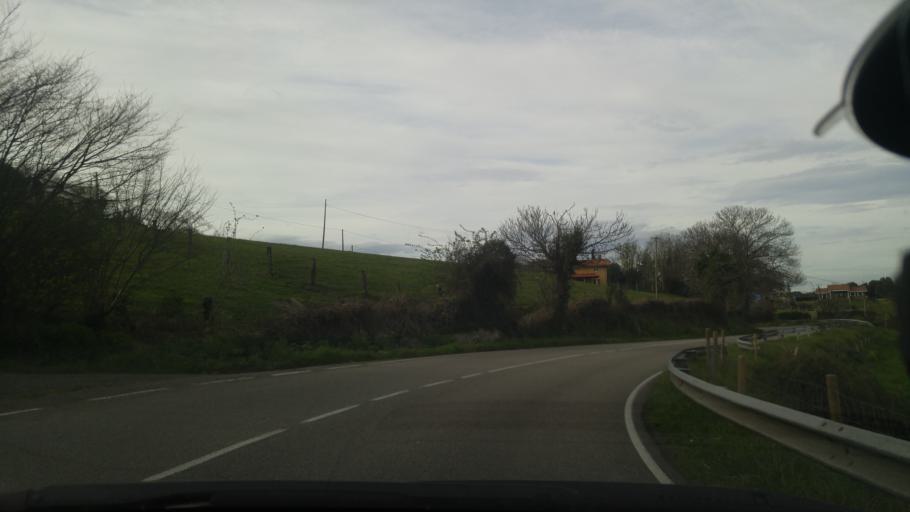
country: ES
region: Asturias
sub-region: Province of Asturias
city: Corvera de Asturias
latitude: 43.4721
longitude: -5.8463
